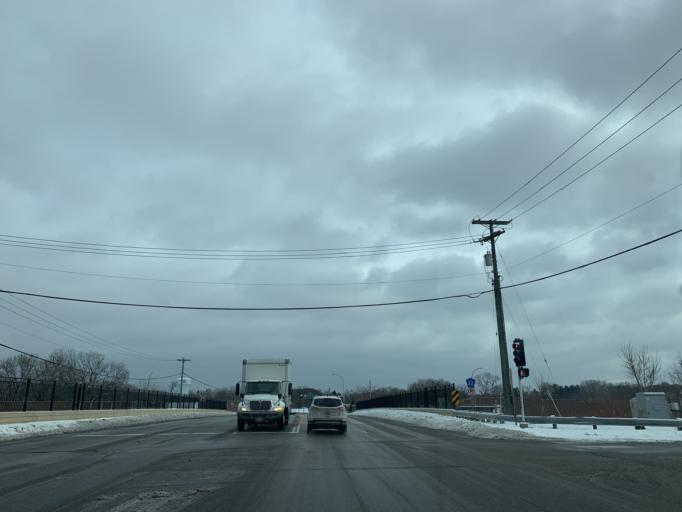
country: US
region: Minnesota
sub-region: Ramsey County
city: Little Canada
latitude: 45.0231
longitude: -93.0906
